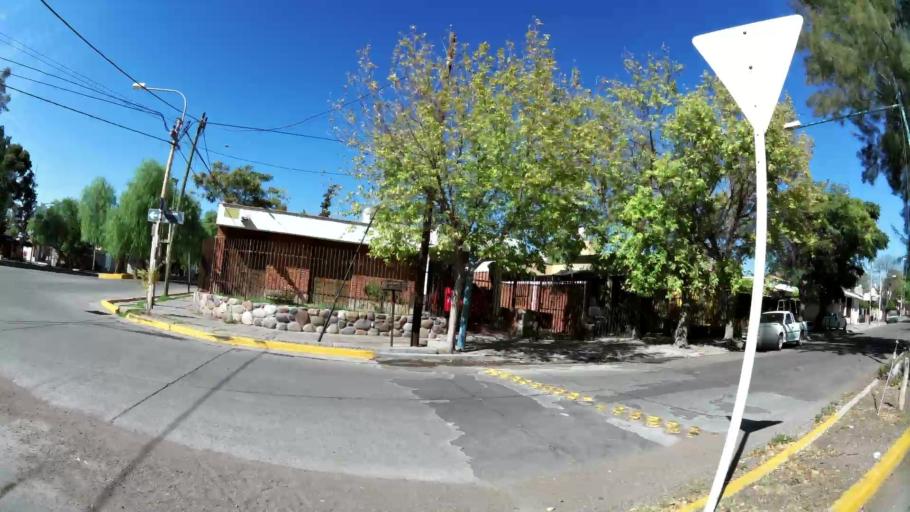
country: AR
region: Mendoza
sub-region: Departamento de Godoy Cruz
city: Godoy Cruz
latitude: -32.9009
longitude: -68.8863
